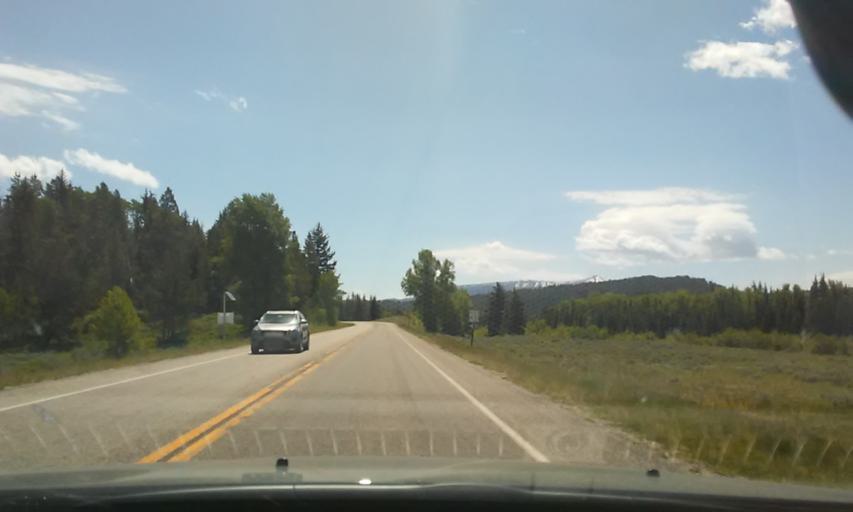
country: US
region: Wyoming
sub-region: Teton County
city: Jackson
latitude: 43.8391
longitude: -110.5041
